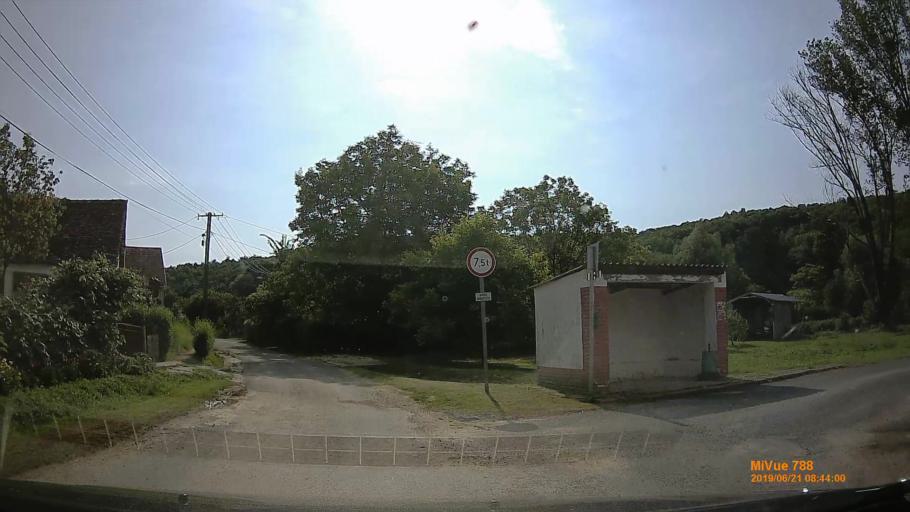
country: HU
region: Baranya
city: Buekkoesd
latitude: 46.1895
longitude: 17.9307
